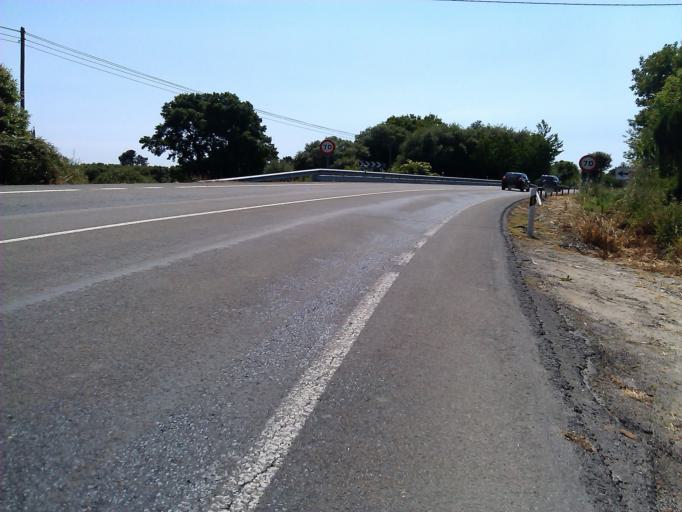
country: ES
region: Galicia
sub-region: Provincia de Lugo
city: Monterroso
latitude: 42.8707
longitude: -7.8845
